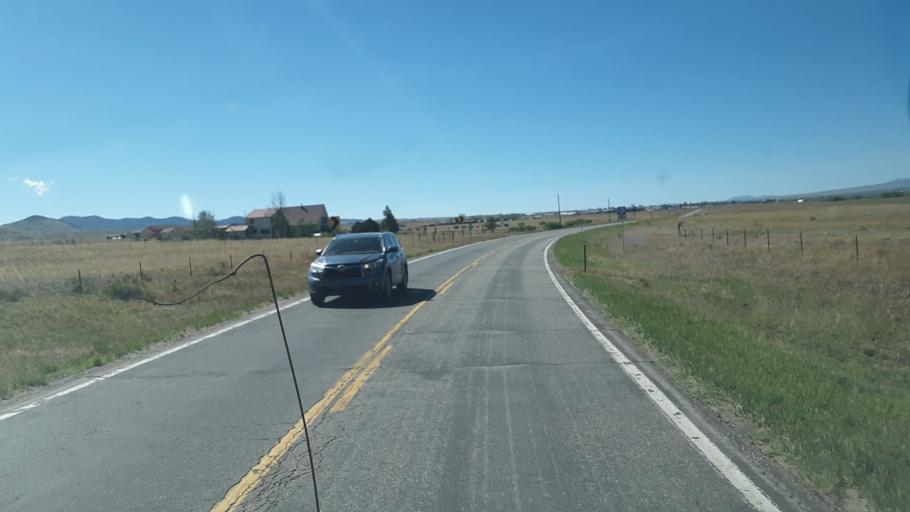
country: US
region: Colorado
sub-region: Custer County
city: Westcliffe
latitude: 38.1635
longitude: -105.4845
